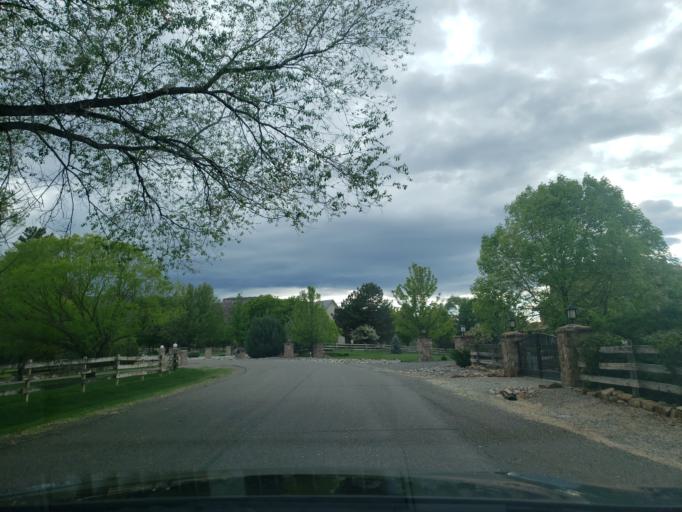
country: US
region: Colorado
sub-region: Mesa County
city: Redlands
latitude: 39.1064
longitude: -108.6784
